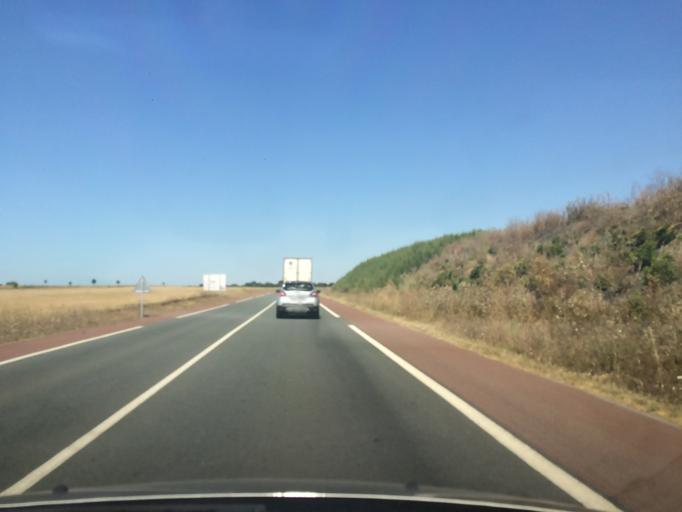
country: FR
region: Poitou-Charentes
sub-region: Departement de la Charente-Maritime
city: Saint-Xandre
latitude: 46.2352
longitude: -1.0751
